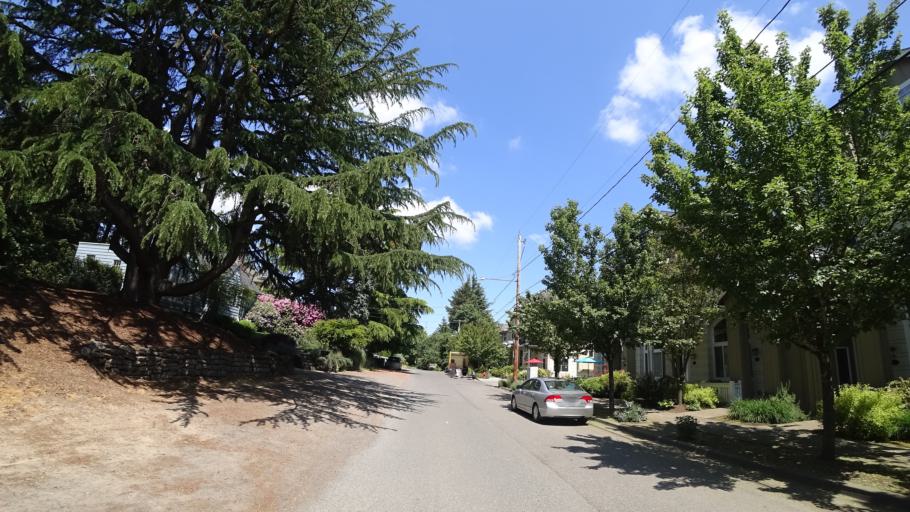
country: US
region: Oregon
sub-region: Clackamas County
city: Lake Oswego
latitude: 45.4644
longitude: -122.7037
